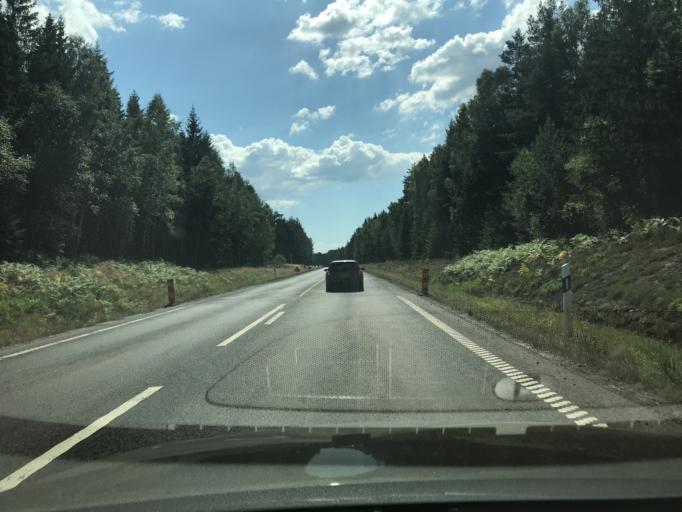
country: SE
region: Kronoberg
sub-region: Almhults Kommun
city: AElmhult
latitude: 56.6452
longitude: 14.2745
